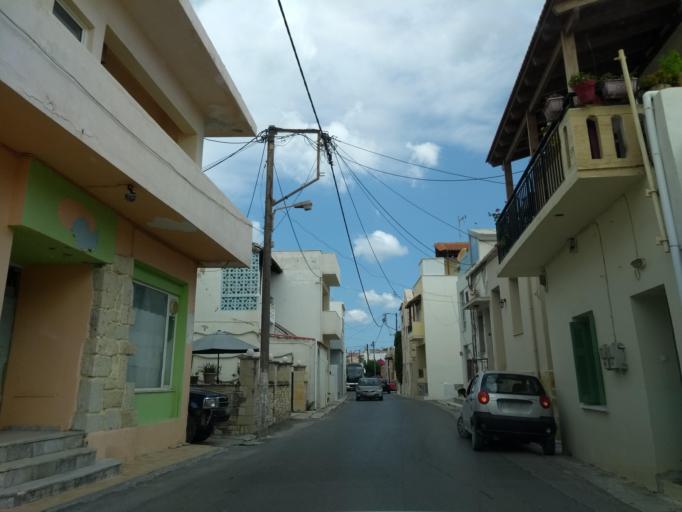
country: GR
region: Crete
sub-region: Nomos Chanias
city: Kalivai
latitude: 35.4556
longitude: 24.1696
